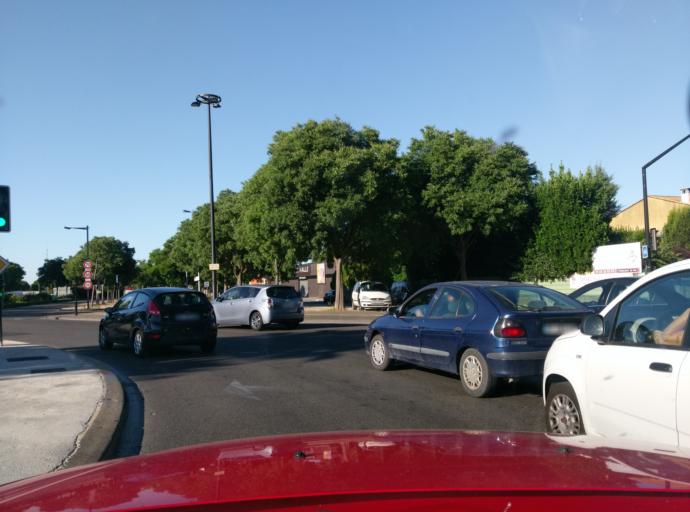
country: FR
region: Languedoc-Roussillon
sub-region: Departement du Gard
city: Nimes
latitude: 43.8370
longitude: 4.3880
